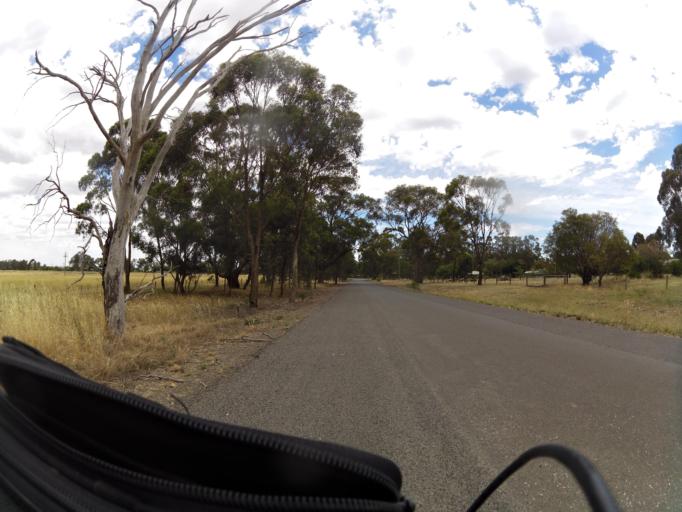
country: AU
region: Victoria
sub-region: Campaspe
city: Kyabram
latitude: -36.7401
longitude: 145.1372
